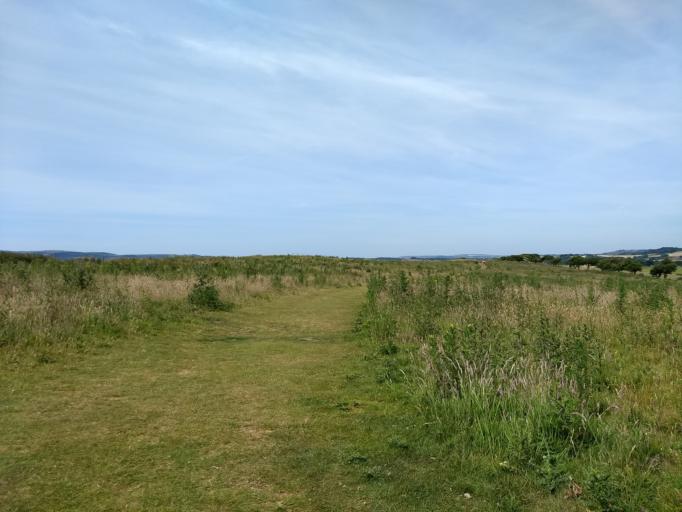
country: GB
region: England
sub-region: Isle of Wight
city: Brading
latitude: 50.6655
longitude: -1.1177
